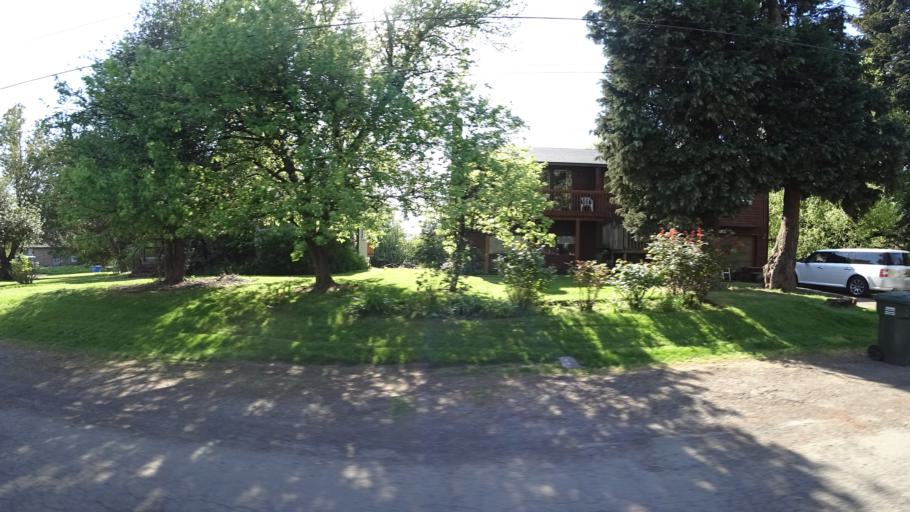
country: US
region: Oregon
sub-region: Clackamas County
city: Milwaukie
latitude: 45.4564
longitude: -122.6327
